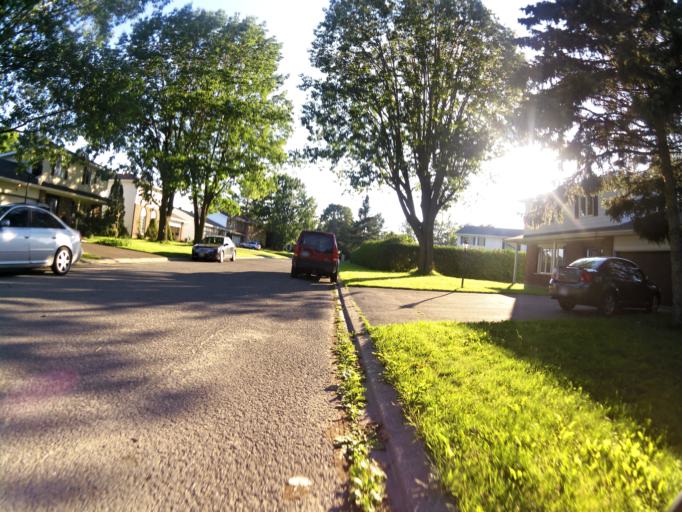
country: CA
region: Ontario
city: Bells Corners
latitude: 45.3301
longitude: -75.7703
